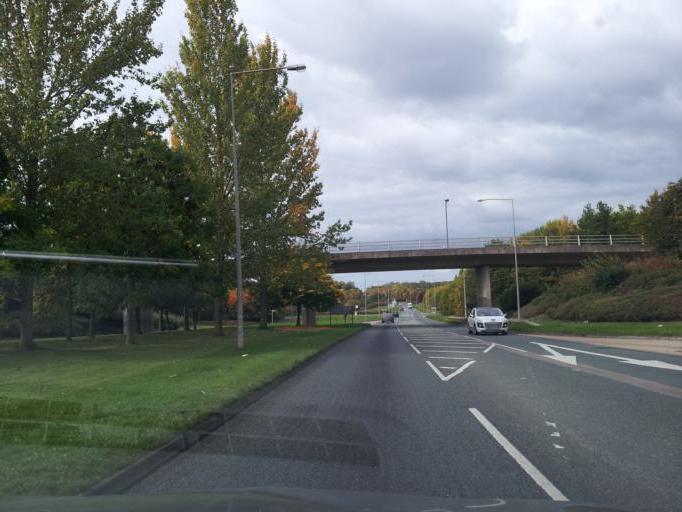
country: GB
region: England
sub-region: Milton Keynes
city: Shenley Church End
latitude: 52.0068
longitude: -0.7930
